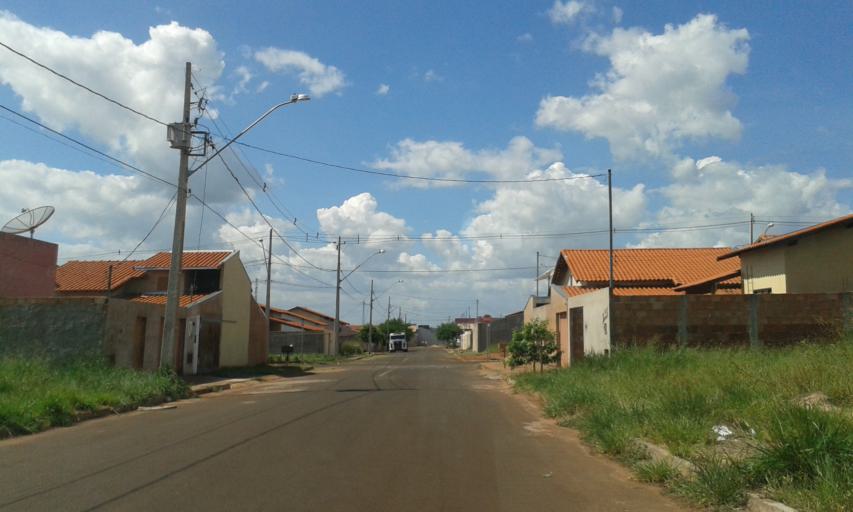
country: BR
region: Minas Gerais
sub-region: Santa Vitoria
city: Santa Vitoria
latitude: -18.8555
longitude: -50.1278
